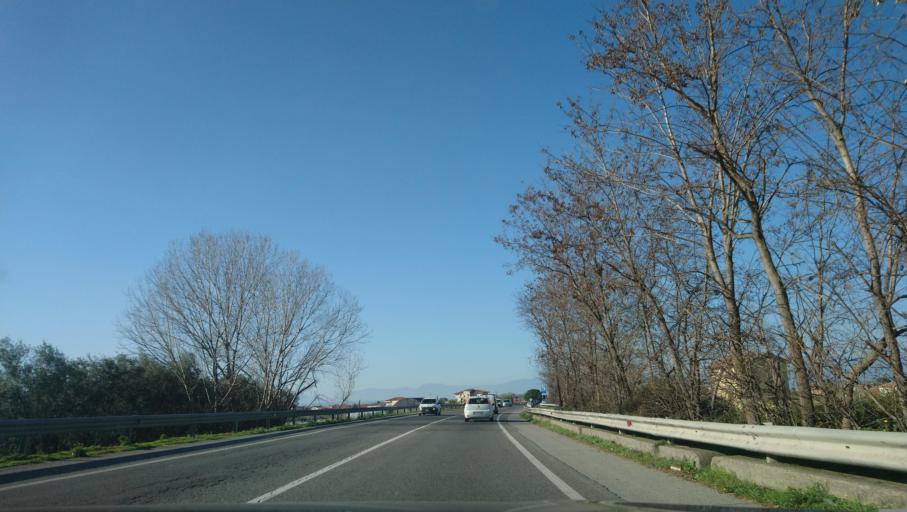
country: IT
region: Calabria
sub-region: Provincia di Cosenza
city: Fabrizio
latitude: 39.6331
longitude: 16.5543
